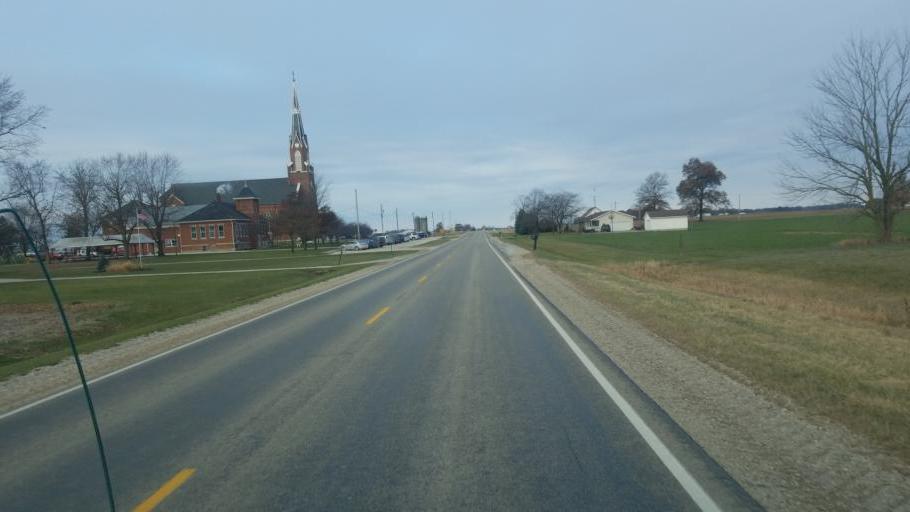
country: US
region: Indiana
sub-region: Adams County
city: Geneva
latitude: 40.5425
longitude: -84.8406
